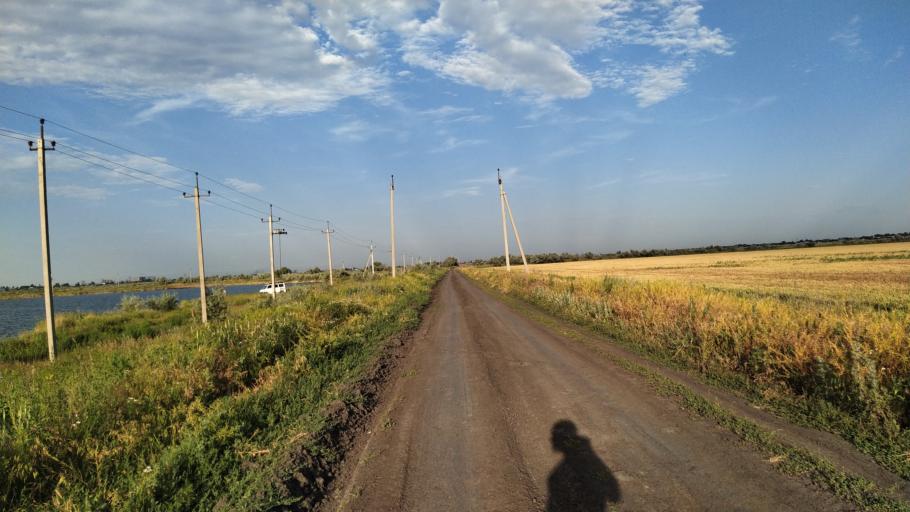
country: RU
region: Rostov
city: Bataysk
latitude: 47.1373
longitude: 39.6512
